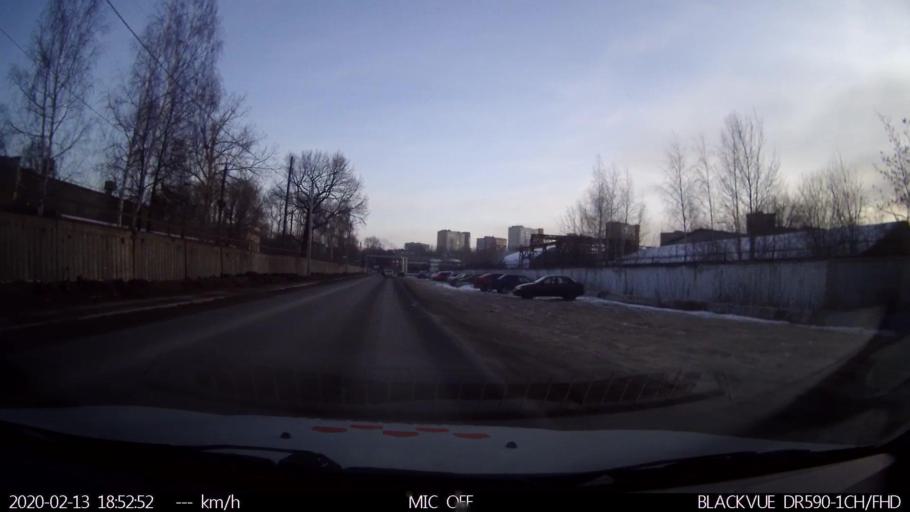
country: RU
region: Nizjnij Novgorod
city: Nizhniy Novgorod
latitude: 56.2707
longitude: 43.9063
